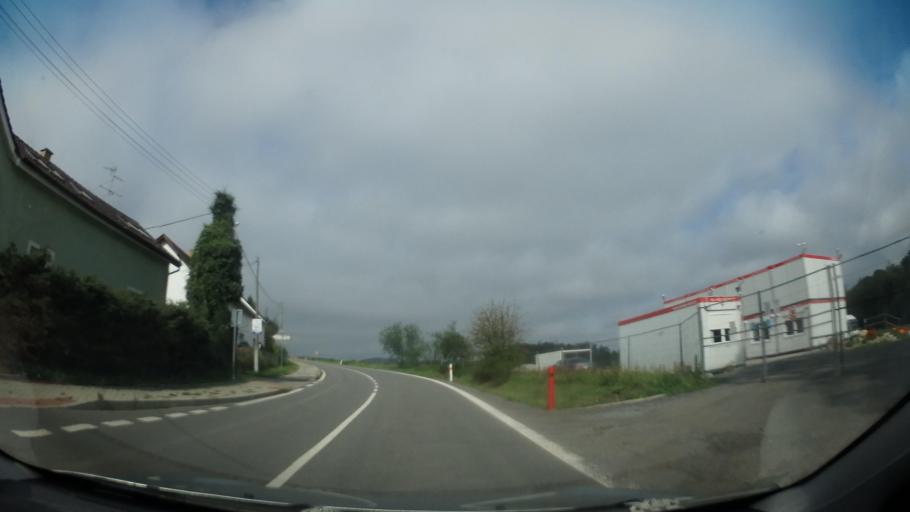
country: CZ
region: Central Bohemia
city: Bystrice
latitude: 49.7588
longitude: 14.6603
